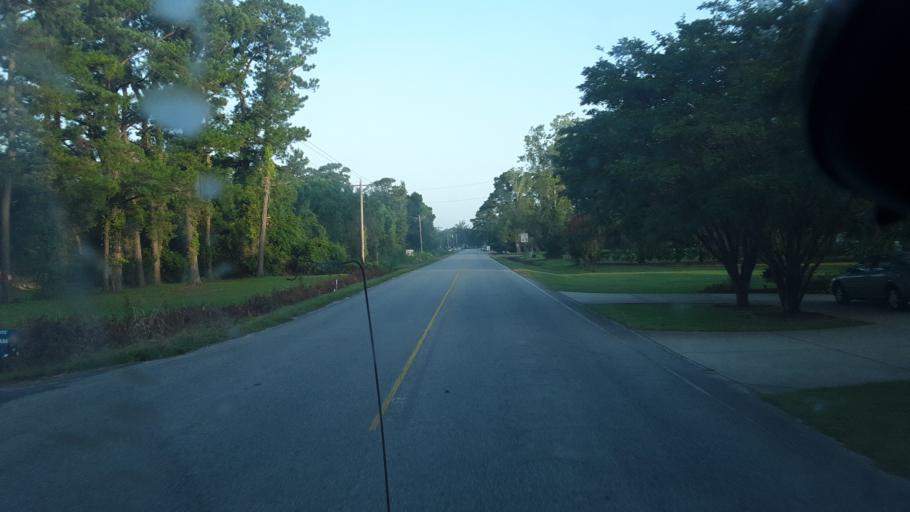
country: US
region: North Carolina
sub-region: Brunswick County
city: Calabash
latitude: 33.8800
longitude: -78.5438
